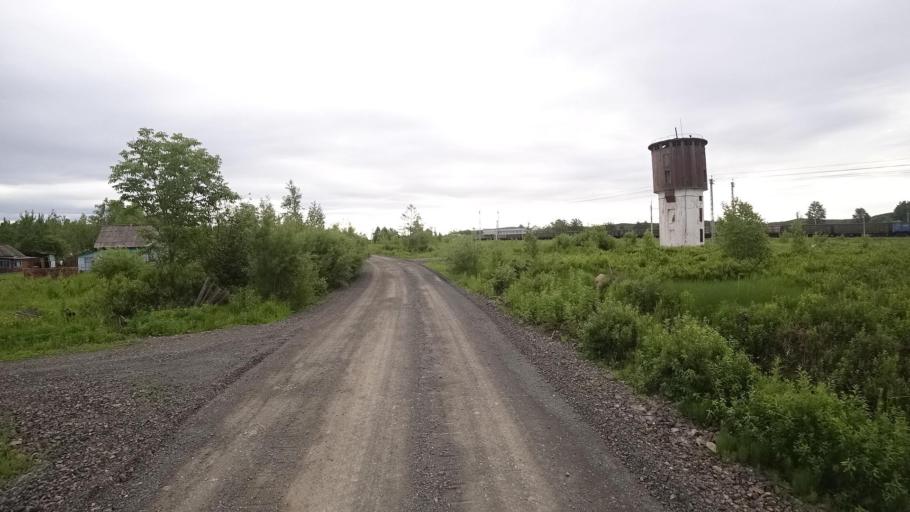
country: RU
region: Khabarovsk Krai
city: Amursk
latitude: 49.9005
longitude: 136.1351
